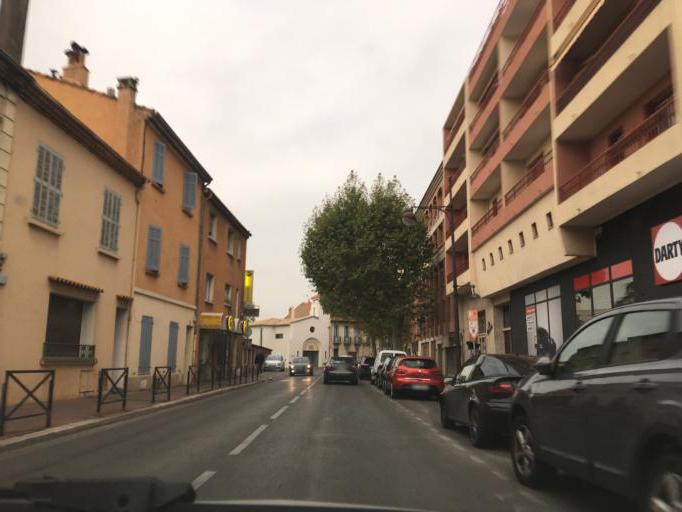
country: FR
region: Provence-Alpes-Cote d'Azur
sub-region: Departement du Var
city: Draguignan
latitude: 43.5353
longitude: 6.4622
